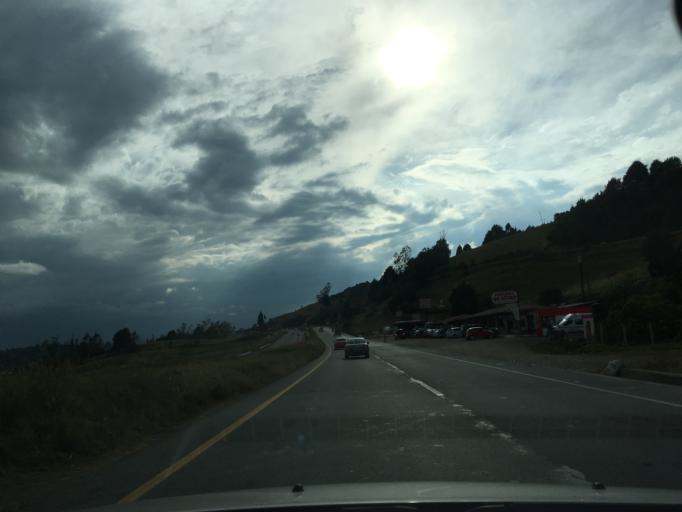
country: CO
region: Boyaca
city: Samaca
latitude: 5.4696
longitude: -73.4110
